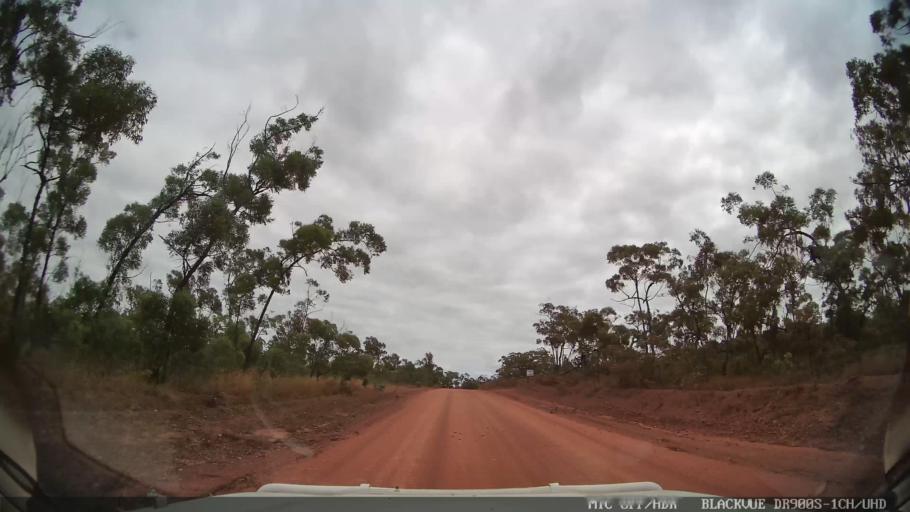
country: AU
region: Queensland
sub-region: Cook
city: Cooktown
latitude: -15.2672
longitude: 144.9453
